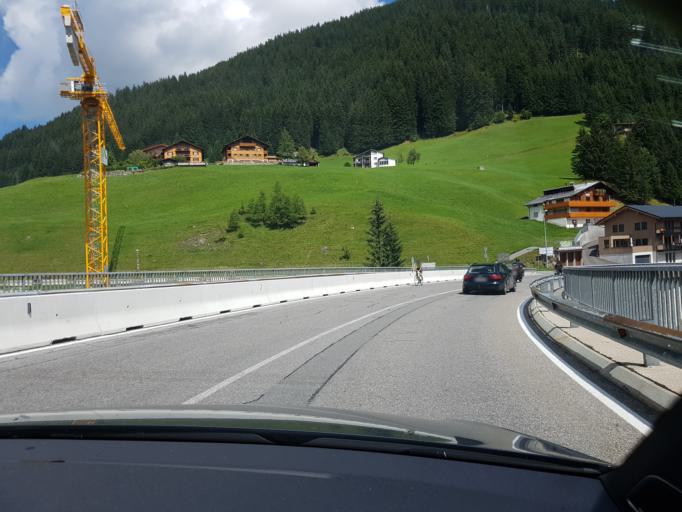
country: AT
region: Vorarlberg
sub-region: Politischer Bezirk Bregenz
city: Damuels
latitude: 47.2834
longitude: 9.8902
